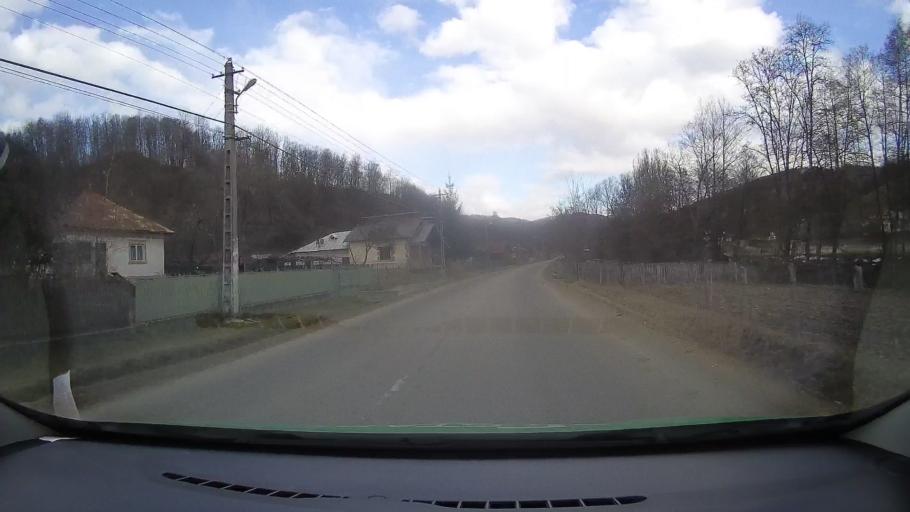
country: RO
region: Dambovita
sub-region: Comuna Visinesti
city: Visinesti
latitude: 45.0681
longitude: 25.5466
